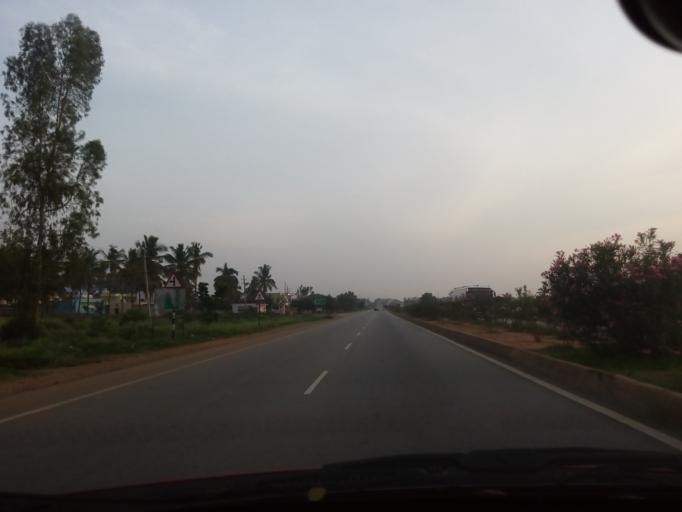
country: IN
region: Karnataka
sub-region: Bangalore Rural
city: Vijayapura
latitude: 13.3401
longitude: 77.7255
